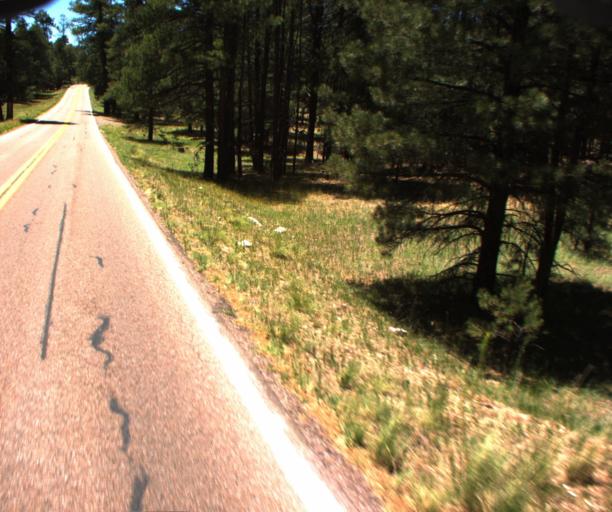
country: US
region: Arizona
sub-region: Gila County
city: Pine
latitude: 34.5422
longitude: -111.3258
